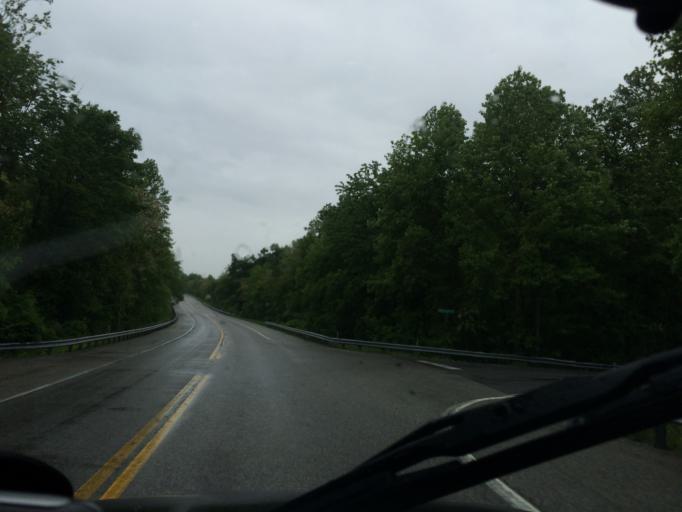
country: US
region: Maryland
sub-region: Washington County
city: Smithsburg
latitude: 39.6660
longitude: -77.5480
